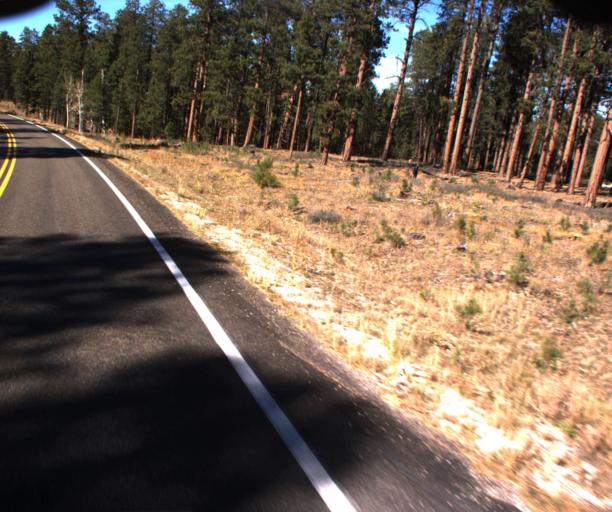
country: US
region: Arizona
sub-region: Coconino County
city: Fredonia
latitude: 36.6642
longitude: -112.1916
